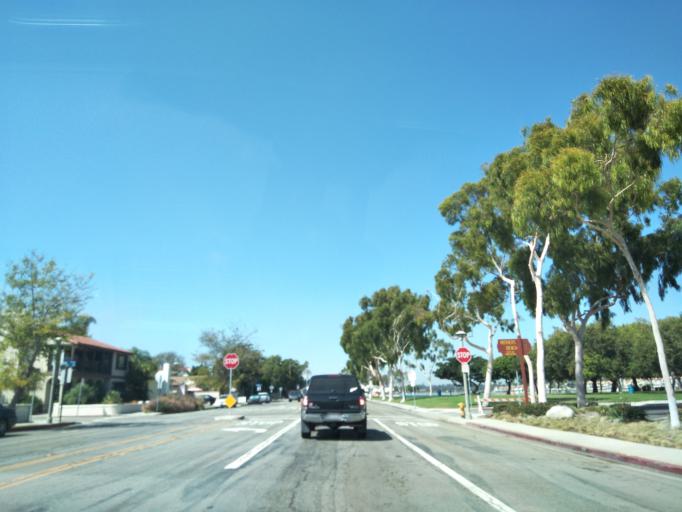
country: US
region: California
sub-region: Orange County
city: Seal Beach
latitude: 33.7579
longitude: -118.1206
